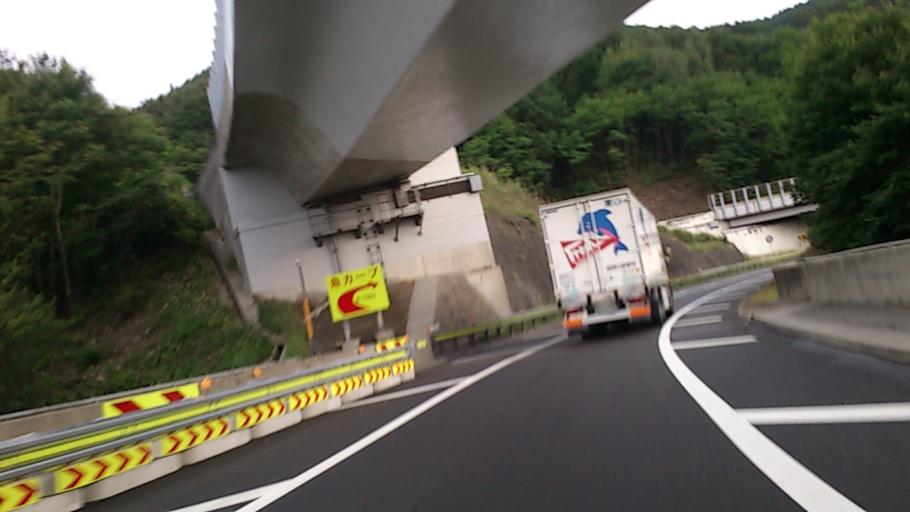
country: JP
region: Nagano
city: Okaya
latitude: 36.0532
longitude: 138.0437
